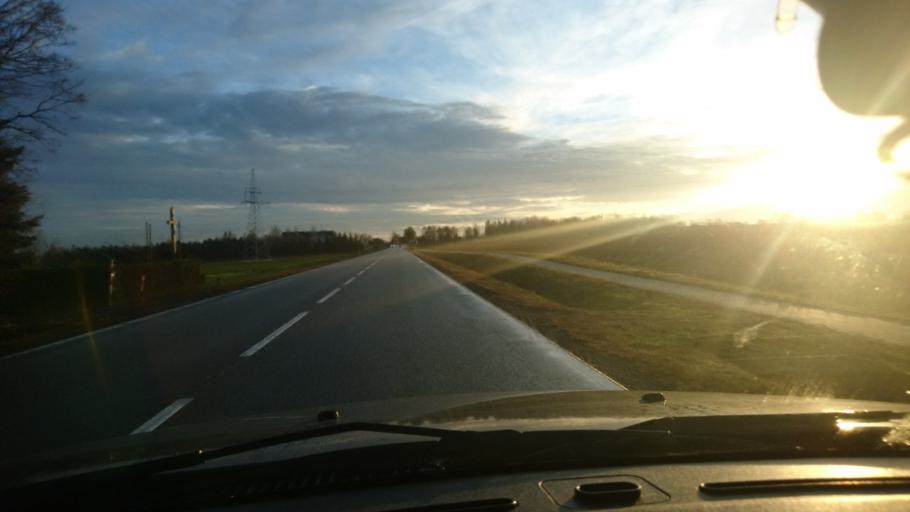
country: PL
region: Greater Poland Voivodeship
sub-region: Powiat kepinski
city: Opatow
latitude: 51.1874
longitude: 18.1470
